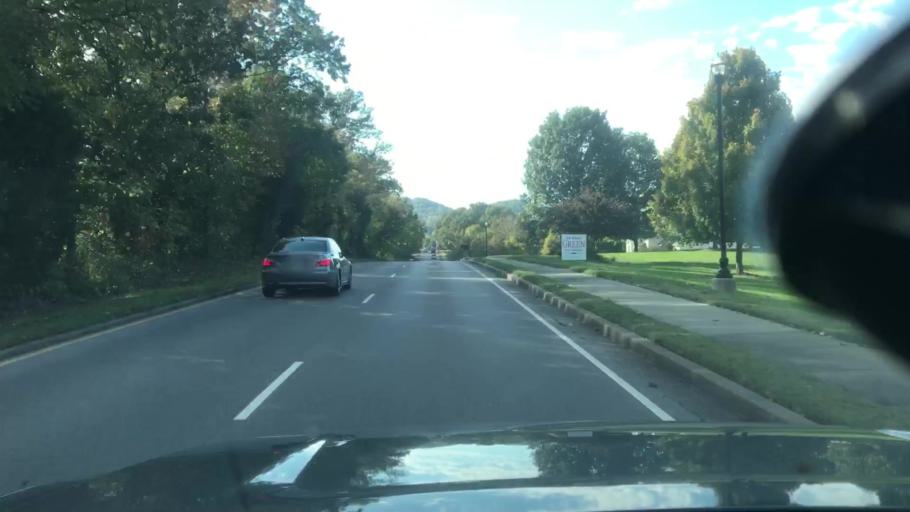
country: US
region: Tennessee
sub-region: Williamson County
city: Brentwood Estates
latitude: 36.0141
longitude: -86.8067
